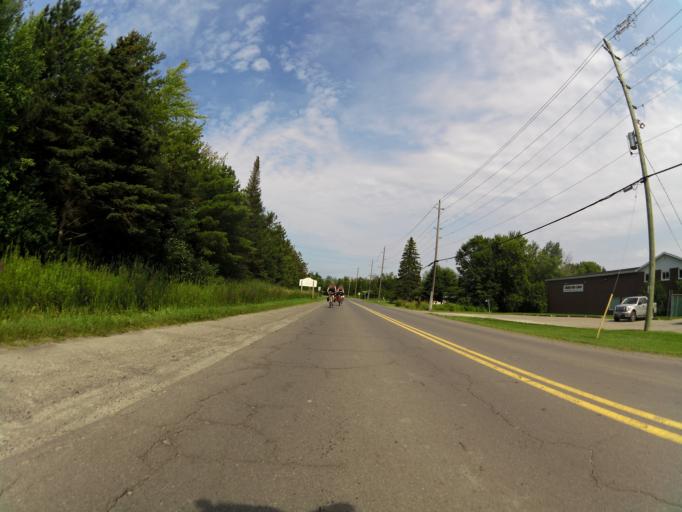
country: CA
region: Ontario
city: Prescott
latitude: 45.0222
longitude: -75.6220
